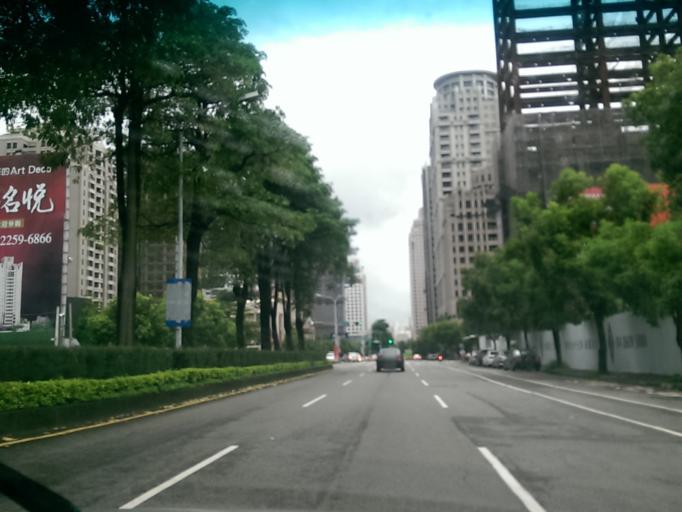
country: TW
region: Taiwan
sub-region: Taichung City
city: Taichung
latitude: 24.1620
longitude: 120.6447
